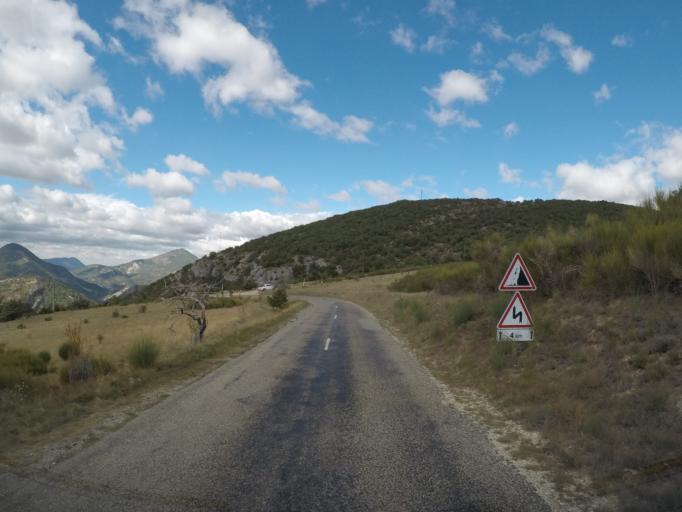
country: FR
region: Provence-Alpes-Cote d'Azur
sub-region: Departement du Vaucluse
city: Sault
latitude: 44.1535
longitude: 5.4477
